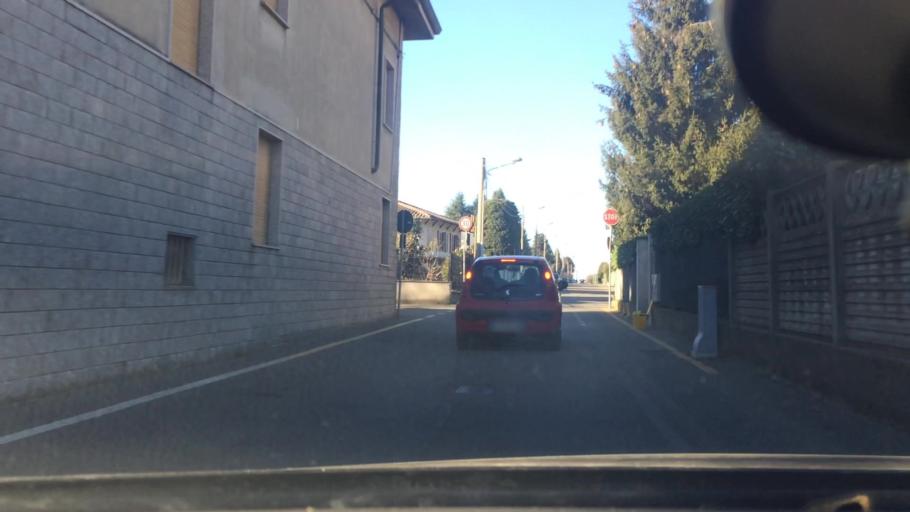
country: IT
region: Lombardy
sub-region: Provincia di Monza e Brianza
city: Ceriano Laghetto
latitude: 45.6263
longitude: 9.0772
